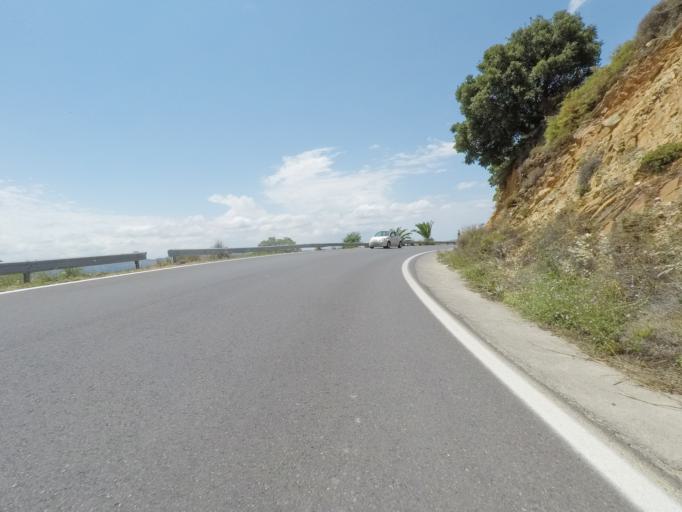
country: GR
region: Crete
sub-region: Nomos Irakleiou
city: Mokhos
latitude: 35.2279
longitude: 25.4603
